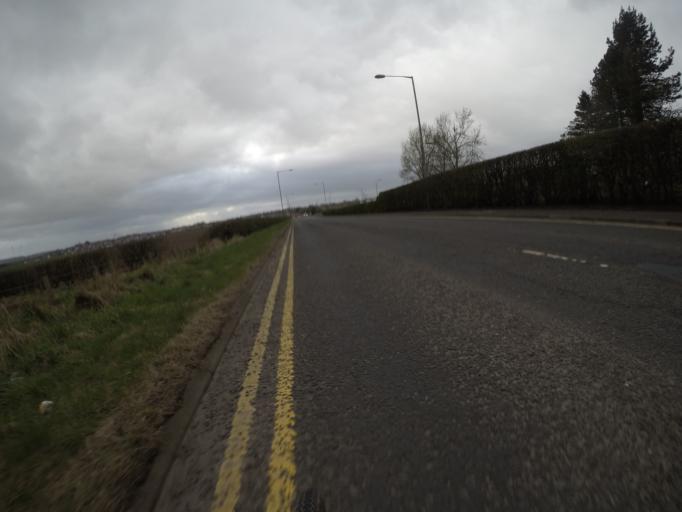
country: GB
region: Scotland
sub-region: East Ayrshire
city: Crosshouse
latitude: 55.6118
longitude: -4.5353
